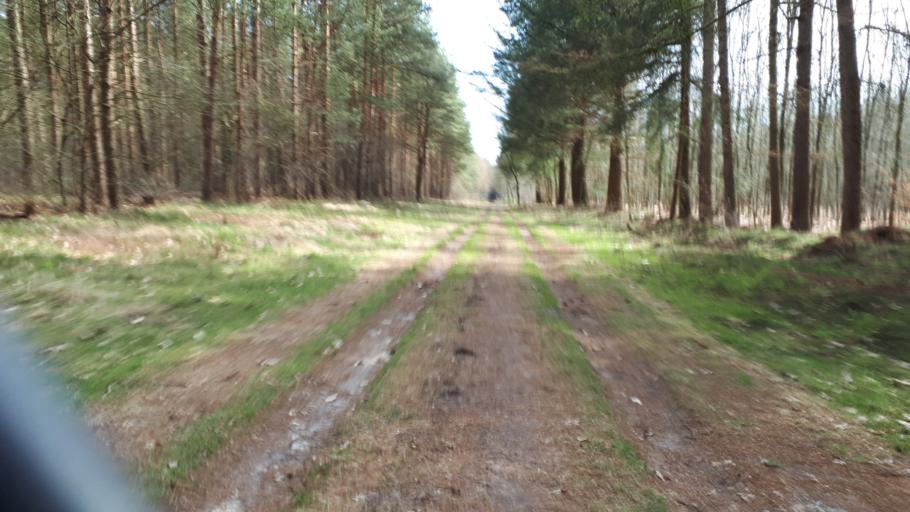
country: DE
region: Lower Saxony
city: Grossenkneten
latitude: 53.0216
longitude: 8.2955
